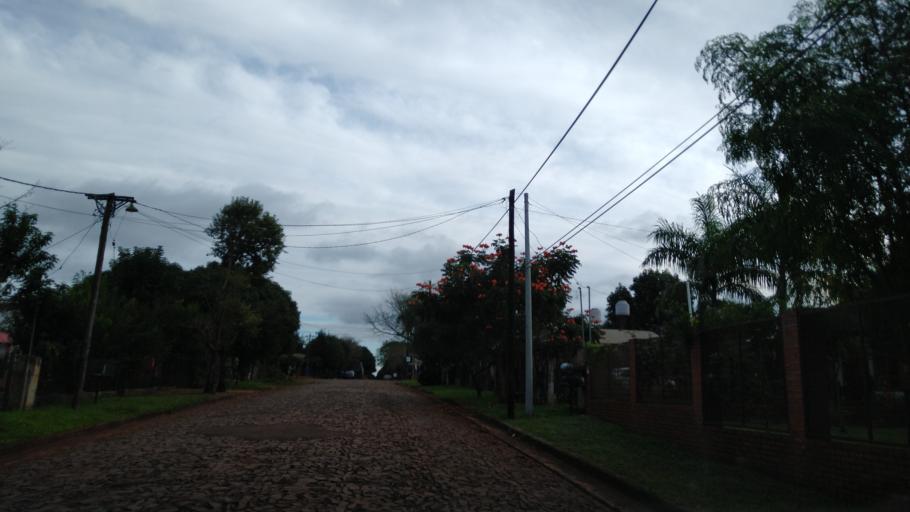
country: AR
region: Misiones
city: Jardin America
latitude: -27.0439
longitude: -55.2403
